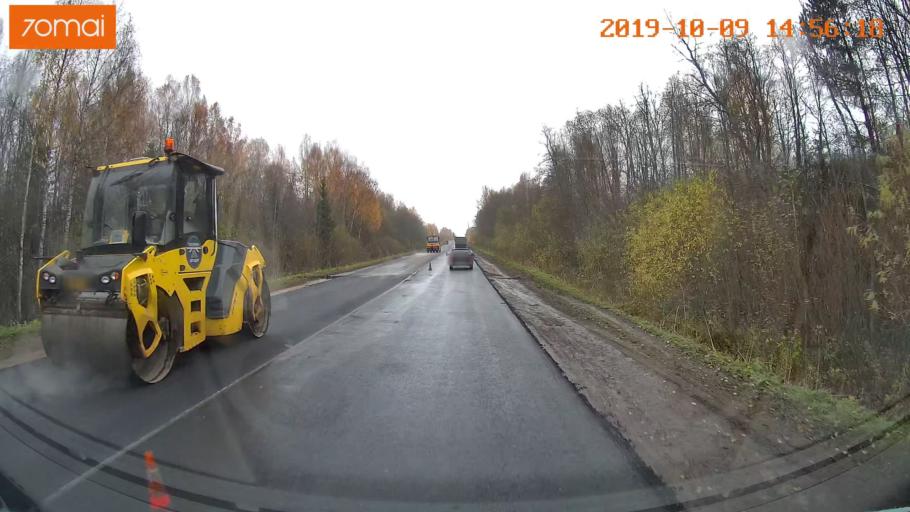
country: RU
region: Kostroma
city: Chistyye Bory
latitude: 58.3466
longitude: 41.6470
